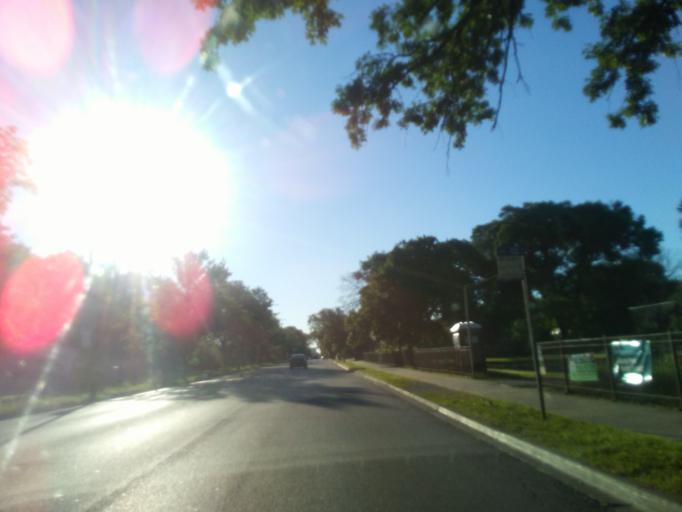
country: US
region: Illinois
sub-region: Cook County
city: Lincolnwood
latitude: 41.9756
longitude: -87.7213
